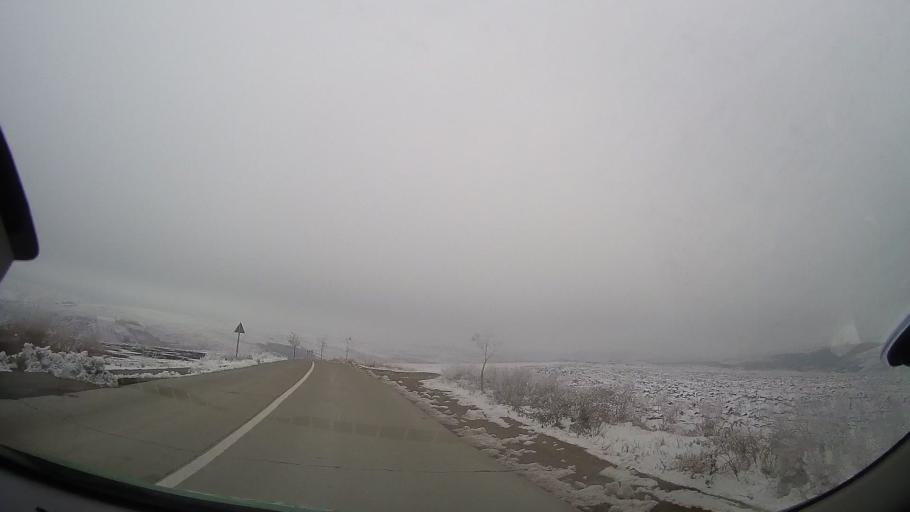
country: RO
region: Vaslui
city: Coroiesti
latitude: 46.2114
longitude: 27.4817
